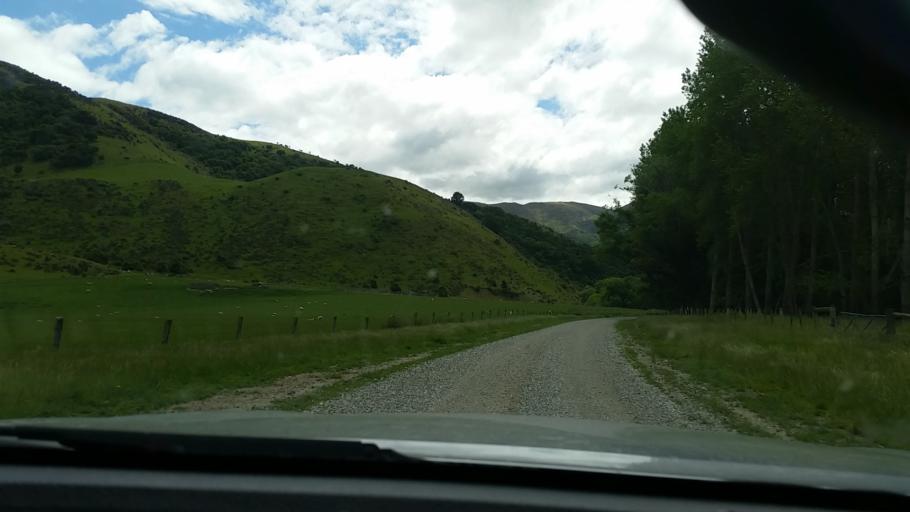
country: NZ
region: Otago
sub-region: Queenstown-Lakes District
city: Kingston
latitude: -45.6828
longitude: 168.6279
